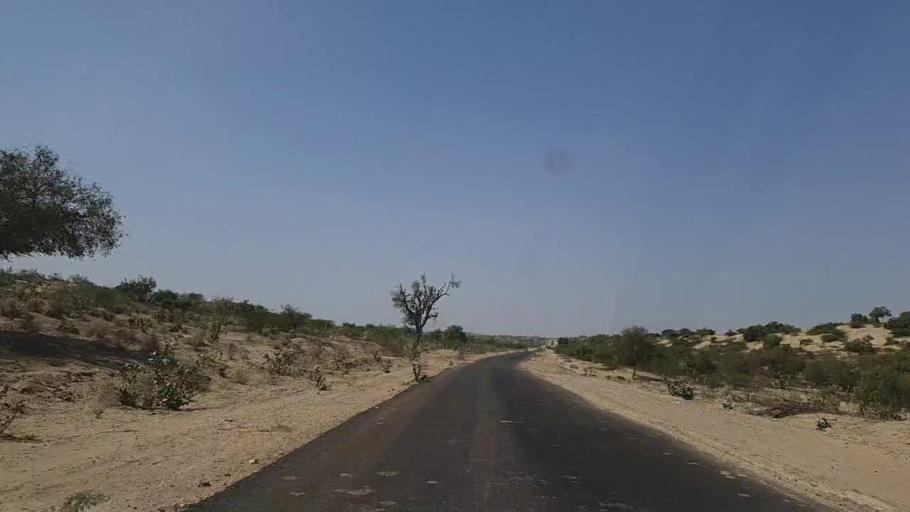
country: PK
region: Sindh
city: Diplo
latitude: 24.5568
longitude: 69.4501
